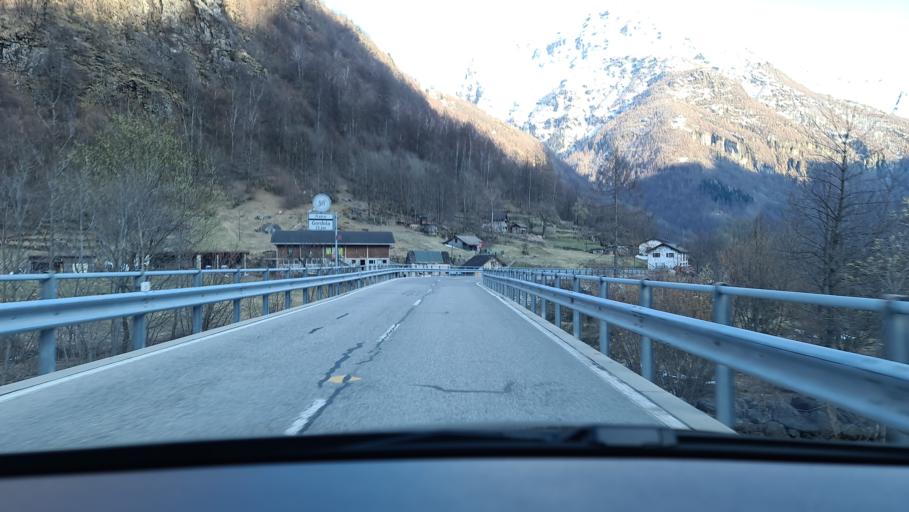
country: CH
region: Ticino
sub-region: Locarno District
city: Lavertezzo
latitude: 46.3496
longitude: 8.7892
